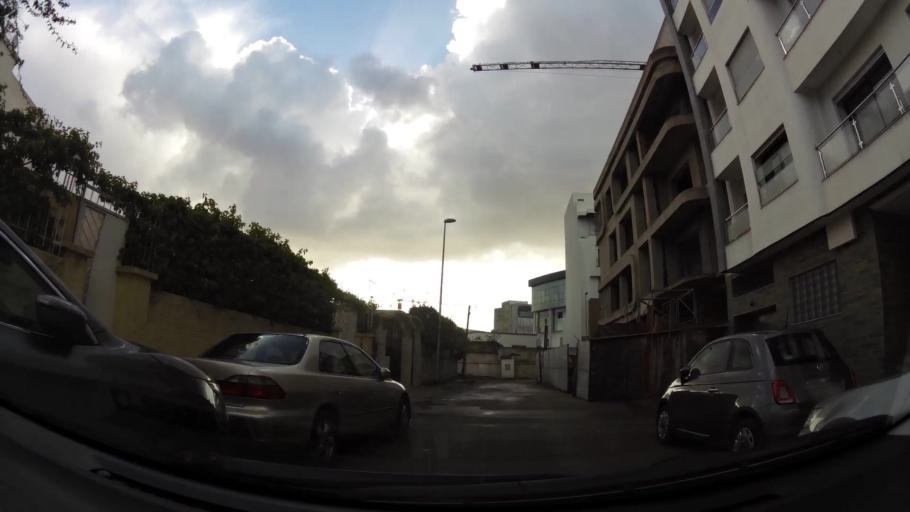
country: MA
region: Grand Casablanca
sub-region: Casablanca
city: Casablanca
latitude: 33.5619
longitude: -7.6457
